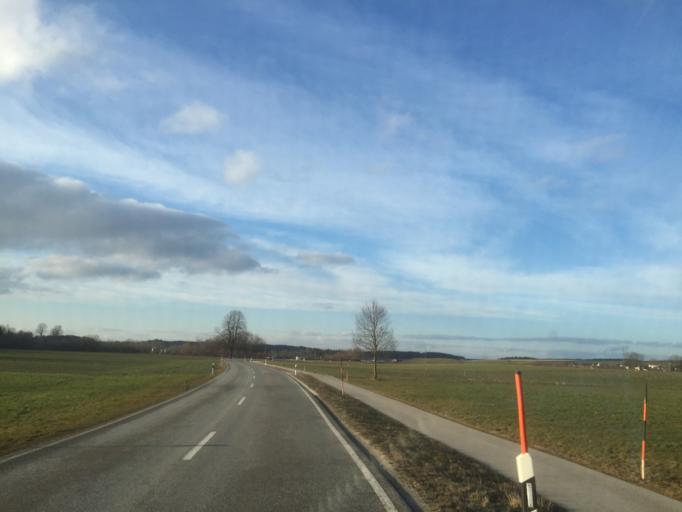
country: DE
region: Bavaria
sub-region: Upper Bavaria
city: Vachendorf
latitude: 47.8556
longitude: 12.5929
